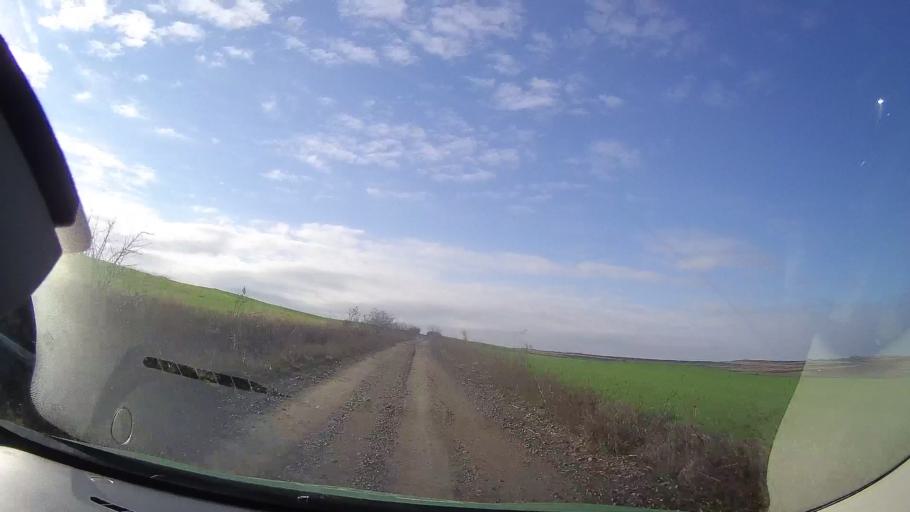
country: RO
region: Mures
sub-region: Comuna Saulia
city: Saulia
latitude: 46.6012
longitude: 24.2380
